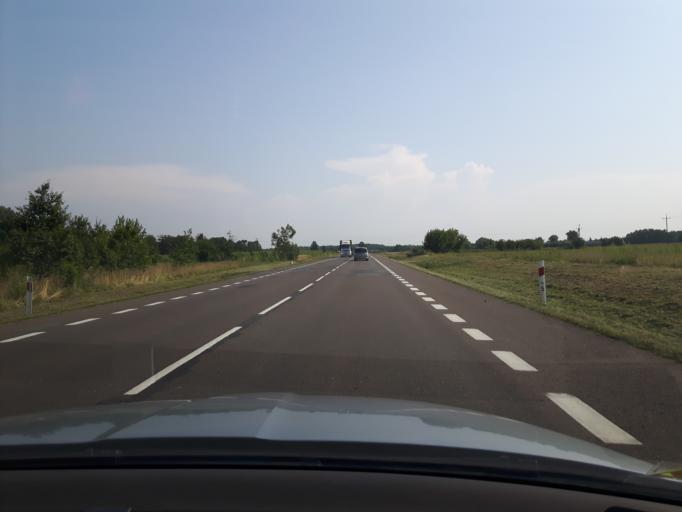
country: PL
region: Masovian Voivodeship
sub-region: Powiat ciechanowski
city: Glinojeck
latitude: 52.7979
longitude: 20.2704
